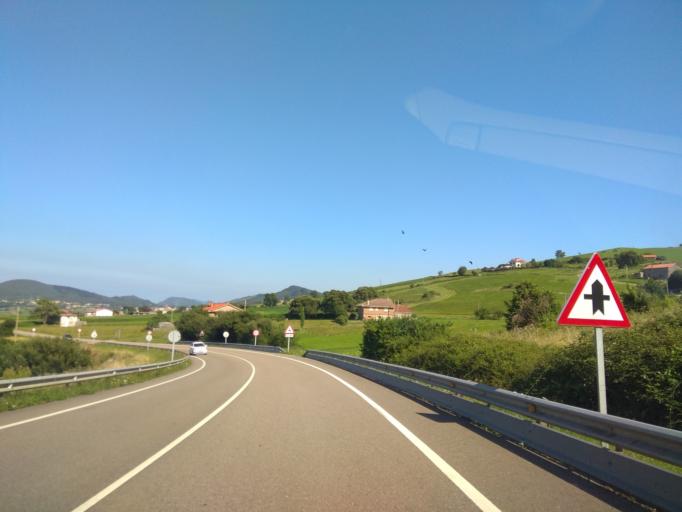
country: ES
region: Cantabria
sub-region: Provincia de Cantabria
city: Bareyo
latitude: 43.4733
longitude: -3.6136
